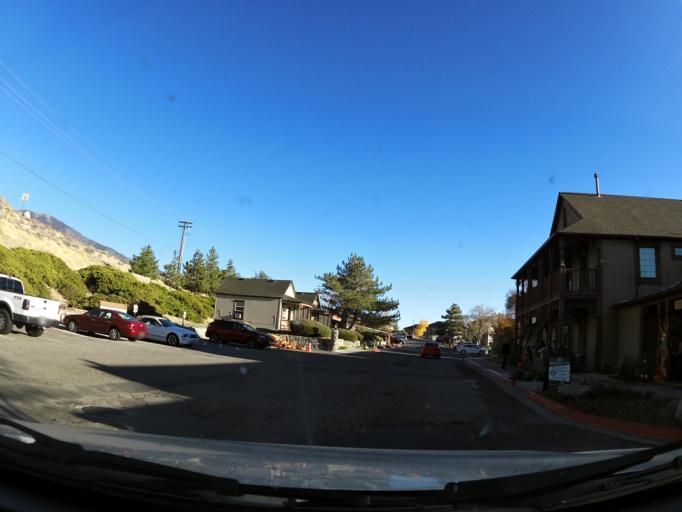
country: US
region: Nevada
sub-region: Douglas County
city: Minden
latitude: 38.9805
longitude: -119.8338
